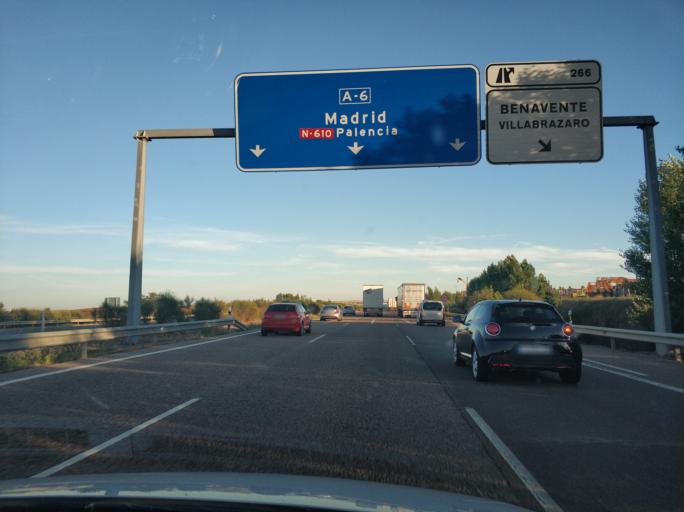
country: ES
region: Castille and Leon
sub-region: Provincia de Zamora
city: Benavente
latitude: 42.0391
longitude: -5.6728
